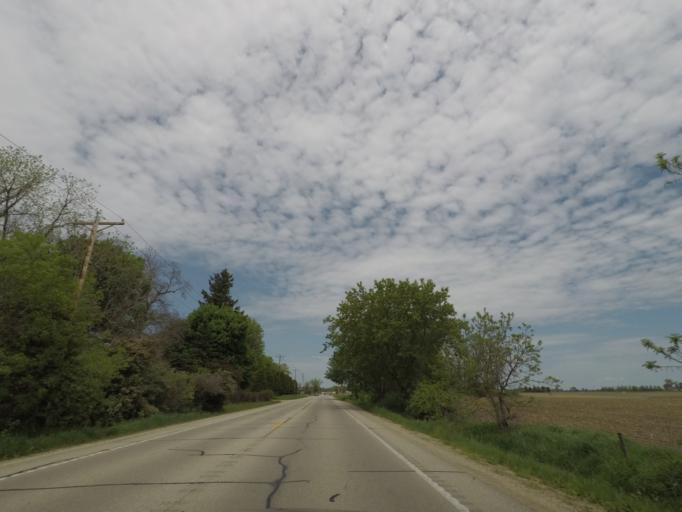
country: US
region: Wisconsin
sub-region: Rock County
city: Evansville
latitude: 42.8041
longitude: -89.2991
